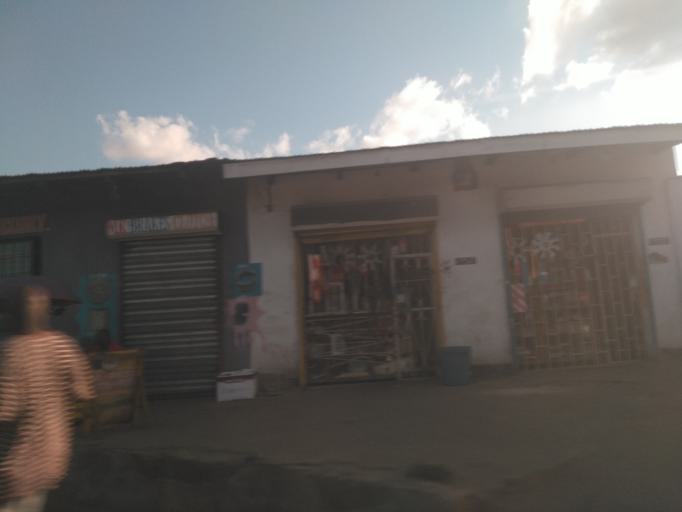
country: TZ
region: Dar es Salaam
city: Dar es Salaam
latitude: -6.8644
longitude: 39.2654
